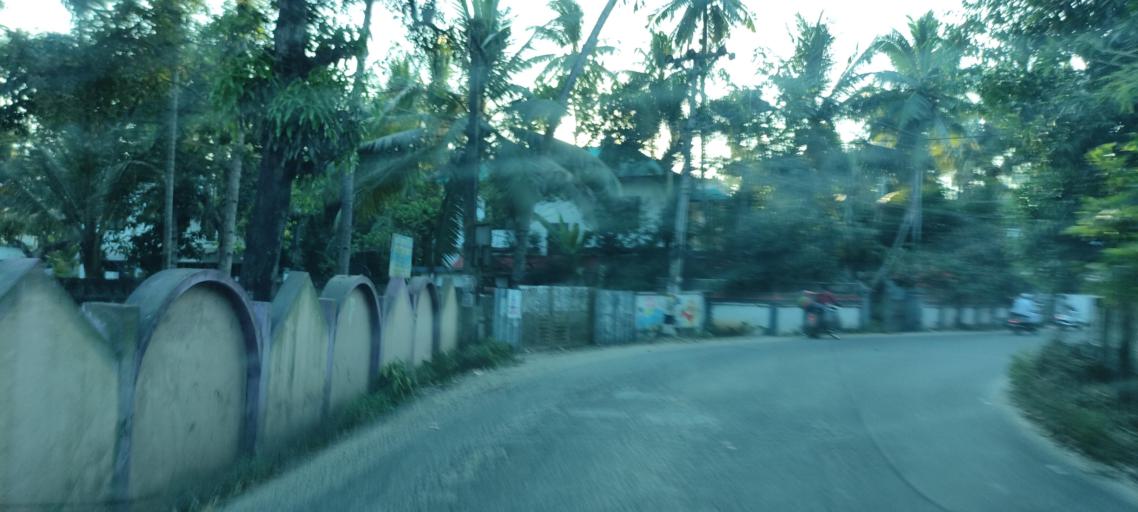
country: IN
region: Kerala
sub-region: Alappuzha
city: Kayankulam
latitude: 9.1768
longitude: 76.4916
